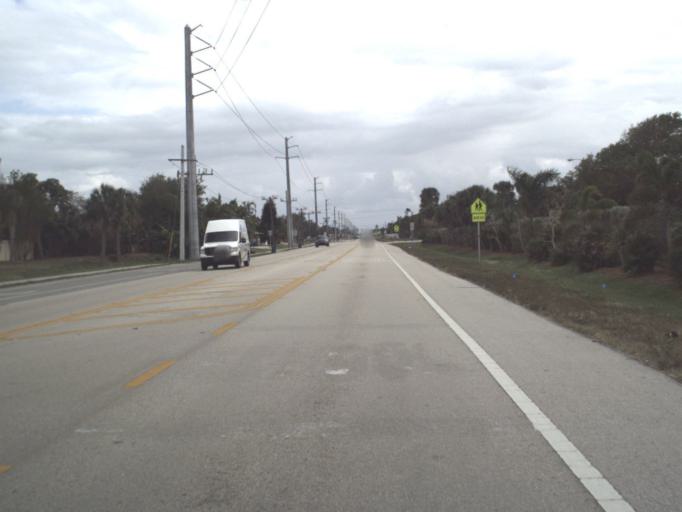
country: US
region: Florida
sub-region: Brevard County
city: South Patrick Shores
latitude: 28.1906
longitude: -80.6063
